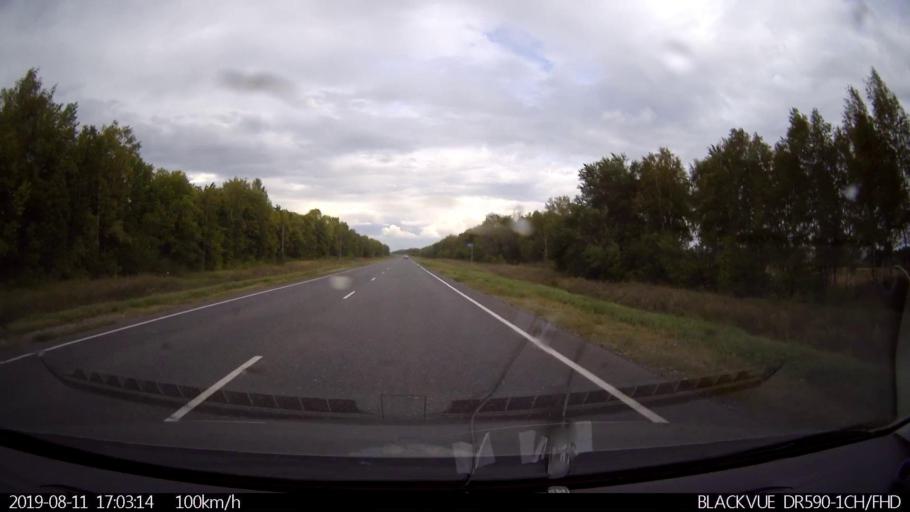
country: RU
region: Ulyanovsk
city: Mayna
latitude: 54.3037
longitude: 47.7343
